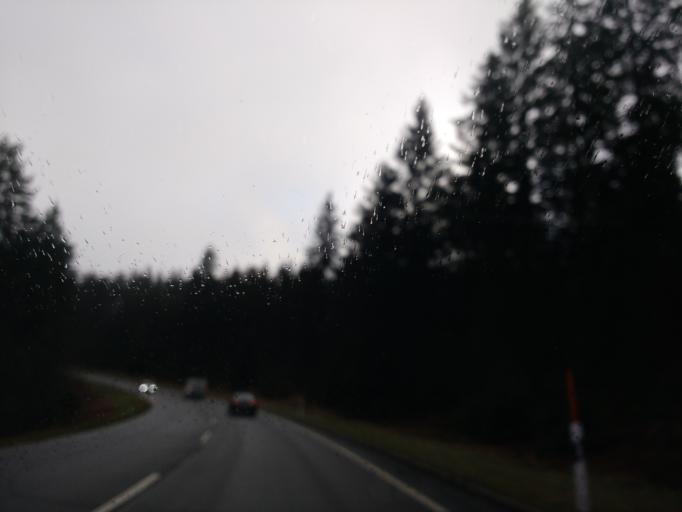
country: DE
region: Baden-Wuerttemberg
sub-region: Freiburg Region
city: Bad Peterstal-Griesbach
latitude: 48.4955
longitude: 8.2438
